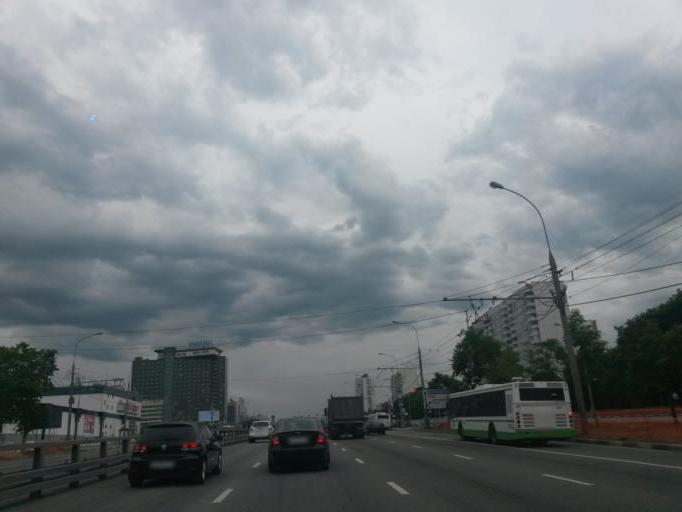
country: RU
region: Moscow
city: Orekhovo-Borisovo
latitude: 55.6227
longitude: 37.7114
